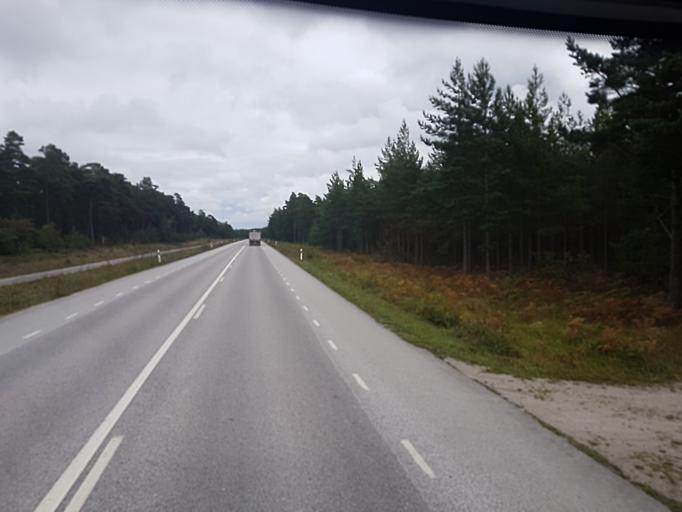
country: SE
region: Gotland
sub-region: Gotland
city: Vibble
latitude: 57.5441
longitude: 18.1939
